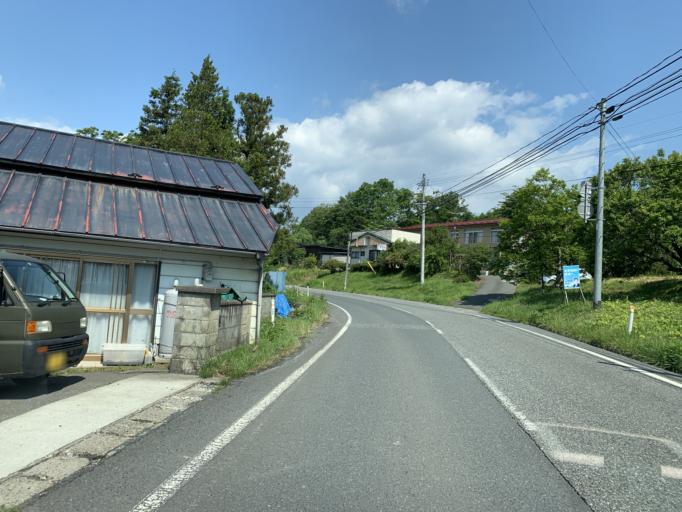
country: JP
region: Iwate
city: Ichinoseki
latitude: 38.8043
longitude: 141.0055
